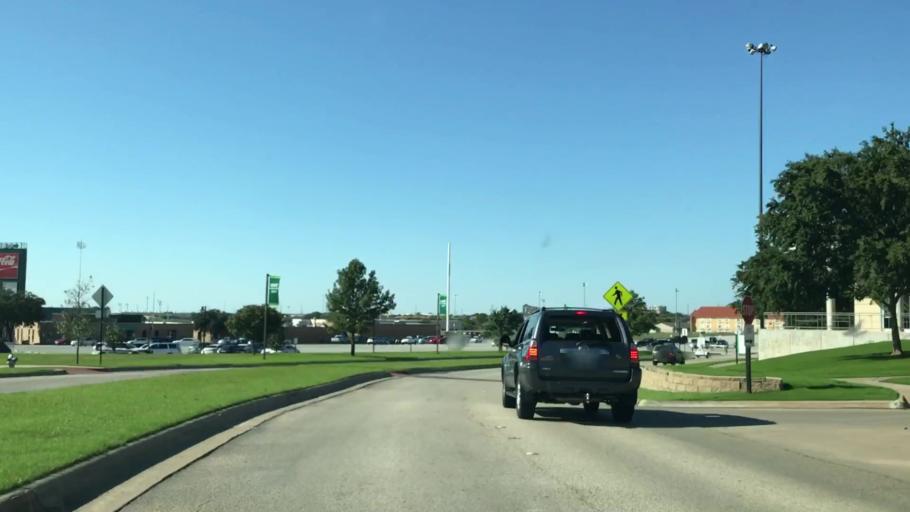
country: US
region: Texas
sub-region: Denton County
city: Denton
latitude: 33.2070
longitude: -97.1545
